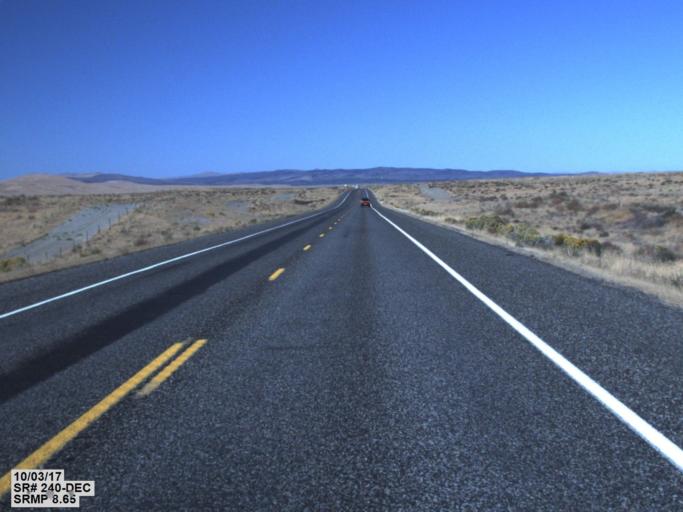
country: US
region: Washington
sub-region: Benton County
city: Benton City
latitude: 46.4967
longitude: -119.6045
